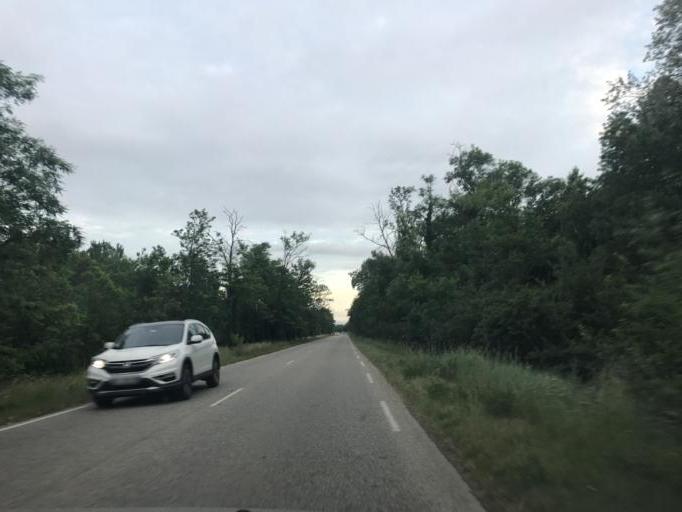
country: FR
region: Rhone-Alpes
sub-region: Departement de l'Ardeche
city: Charmes-sur-Rhone
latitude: 44.8511
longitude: 4.8491
